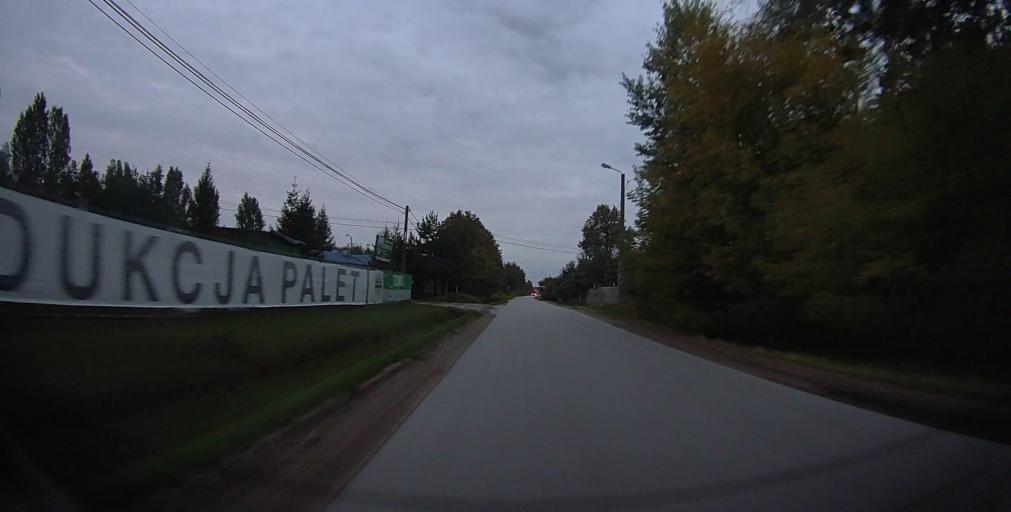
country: PL
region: Masovian Voivodeship
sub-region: Powiat radomski
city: Jedlinsk
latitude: 51.4652
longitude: 21.1281
